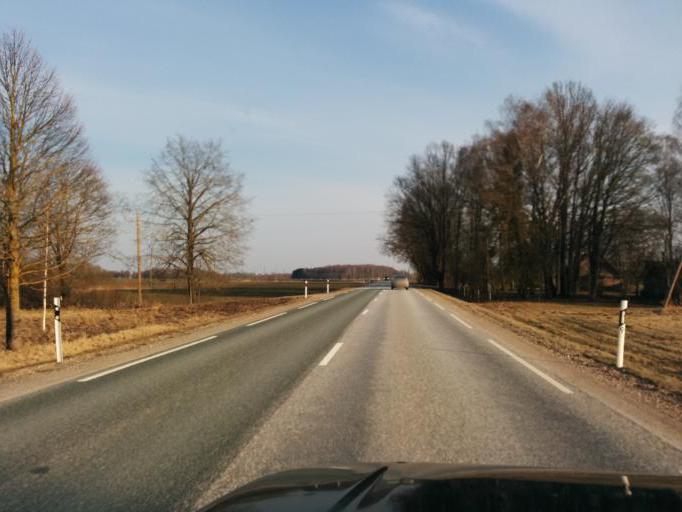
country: LV
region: Lecava
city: Iecava
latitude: 56.5924
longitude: 24.1317
